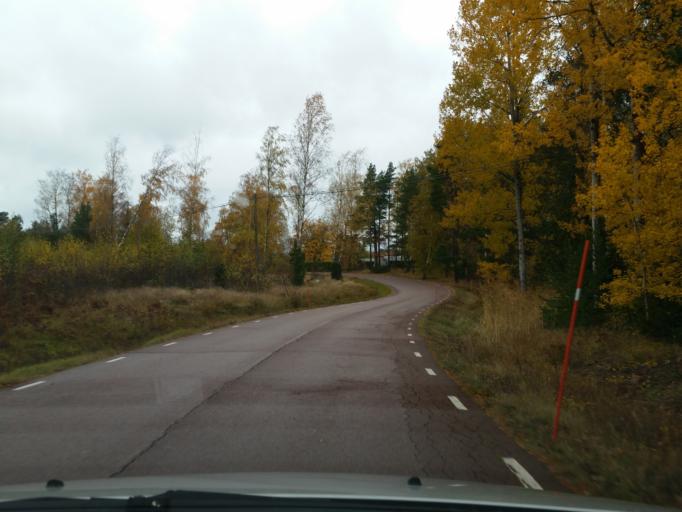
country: AX
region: Alands landsbygd
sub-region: Lumparland
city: Lumparland
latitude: 60.1306
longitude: 20.2678
